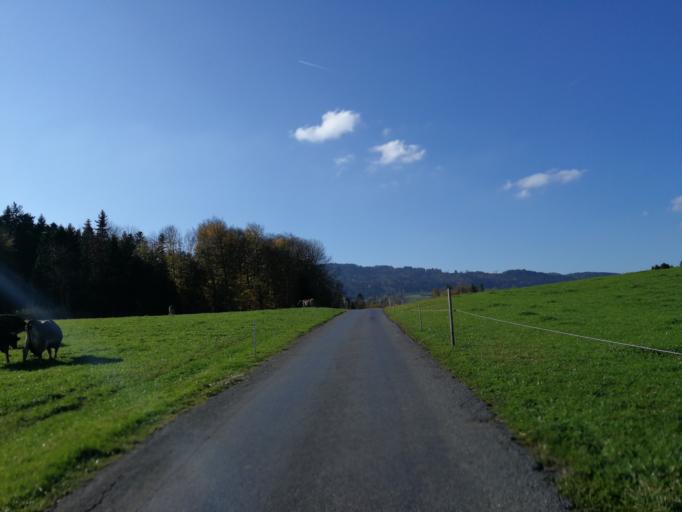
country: CH
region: Zurich
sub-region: Bezirk Uster
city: Esslingen
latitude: 47.2989
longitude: 8.7069
